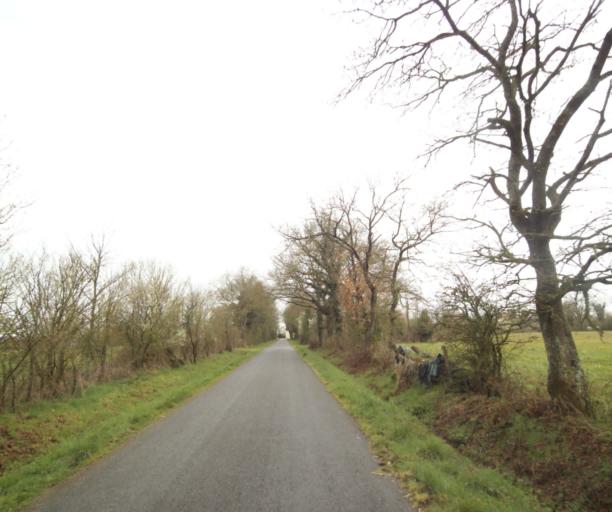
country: FR
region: Pays de la Loire
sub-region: Departement de la Loire-Atlantique
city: Bouvron
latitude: 47.4409
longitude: -1.8512
